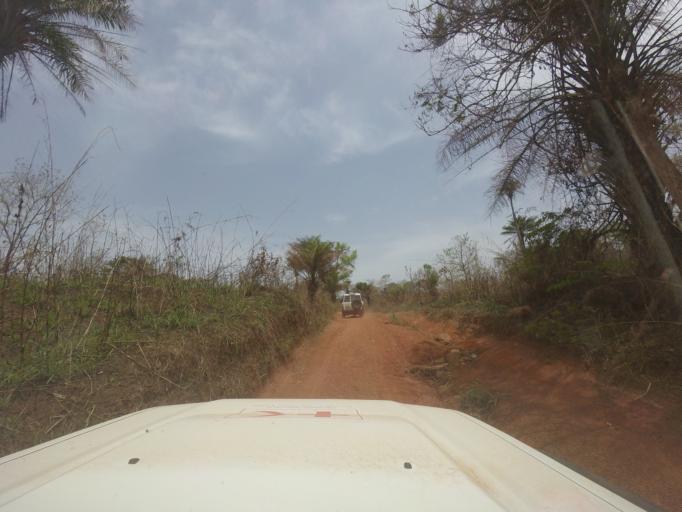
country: SL
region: Eastern Province
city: Buedu
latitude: 8.4704
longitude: -10.3333
